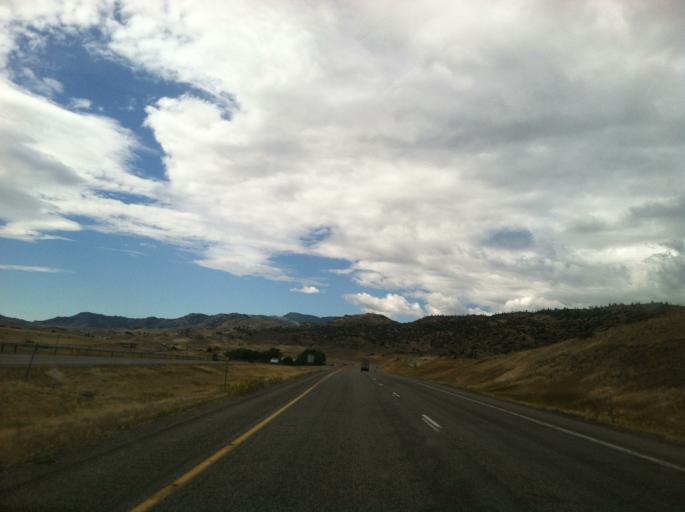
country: US
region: Montana
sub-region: Park County
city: Livingston
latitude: 45.6576
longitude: -110.6306
